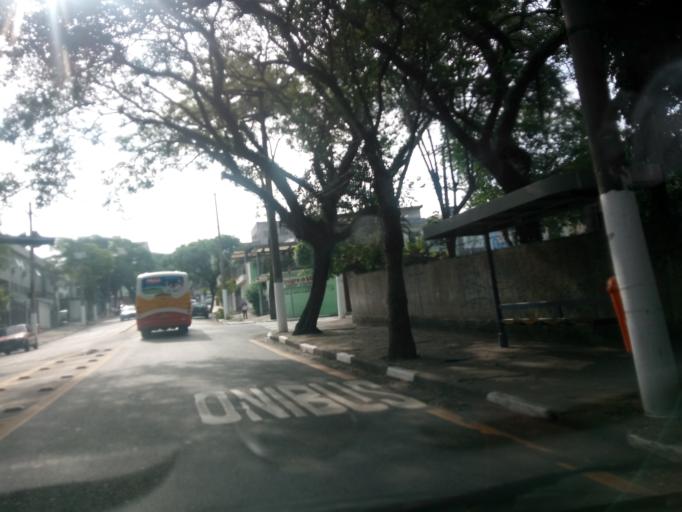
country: BR
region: Sao Paulo
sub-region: Sao Bernardo Do Campo
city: Sao Bernardo do Campo
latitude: -23.6839
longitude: -46.5750
